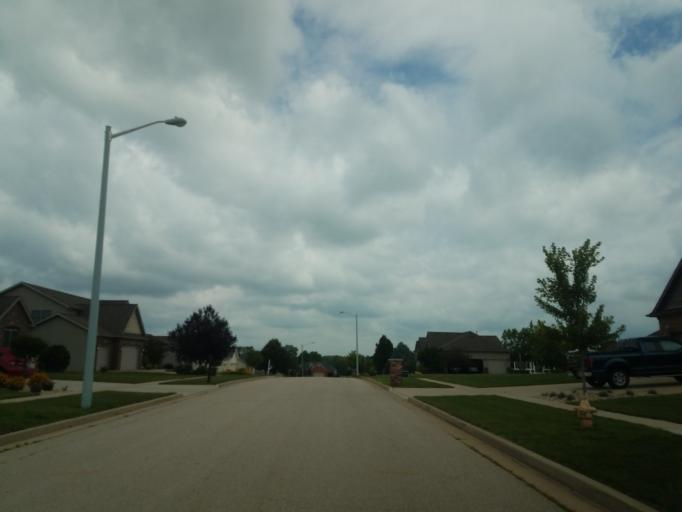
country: US
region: Illinois
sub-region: McLean County
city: Bloomington
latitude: 40.4473
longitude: -89.0382
